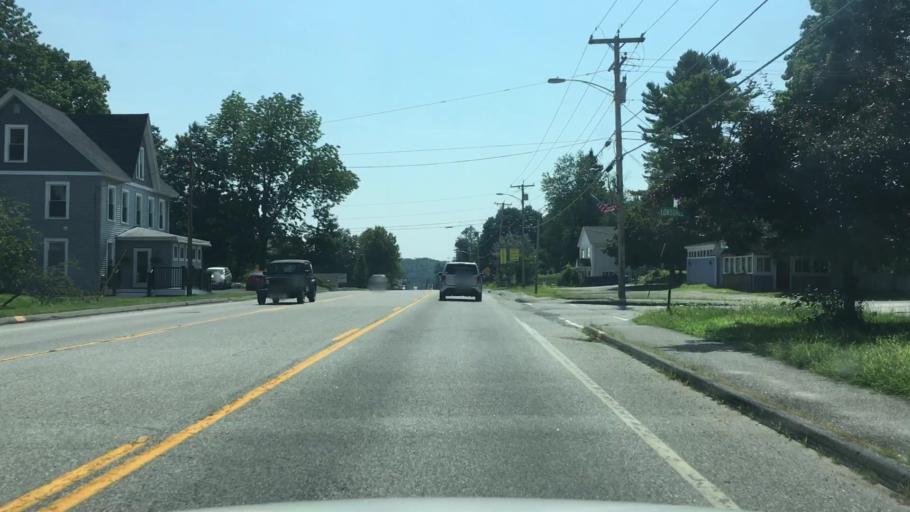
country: US
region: Maine
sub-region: Kennebec County
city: Farmingdale
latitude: 44.2631
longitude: -69.7821
